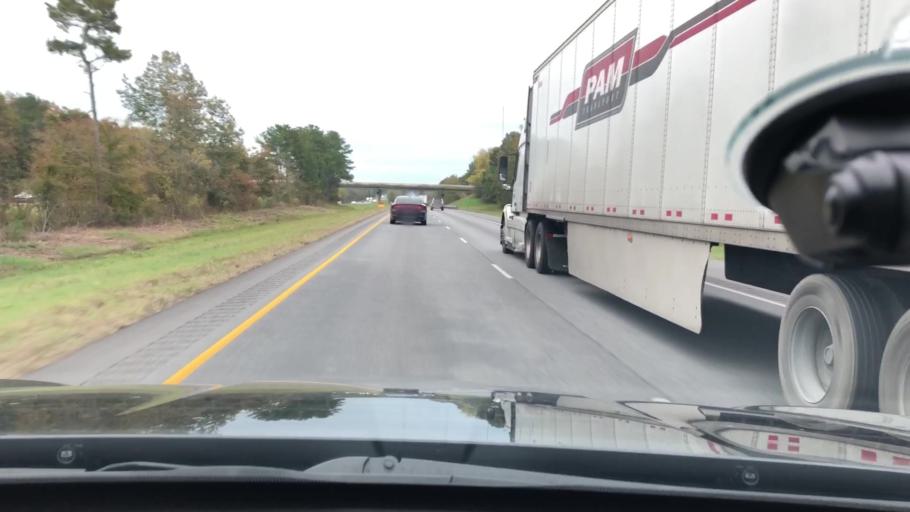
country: US
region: Arkansas
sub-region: Hempstead County
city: Hope
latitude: 33.6231
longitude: -93.7698
